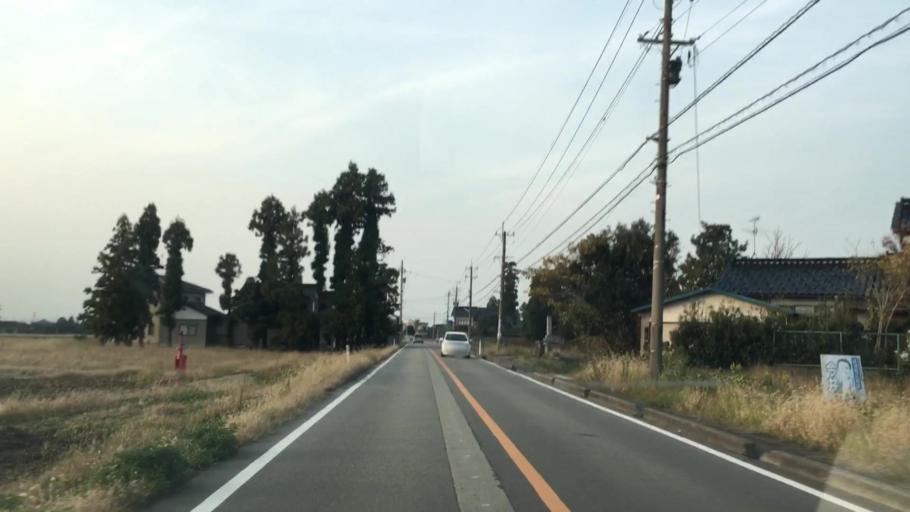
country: JP
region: Toyama
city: Toyama-shi
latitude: 36.6078
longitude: 137.2527
